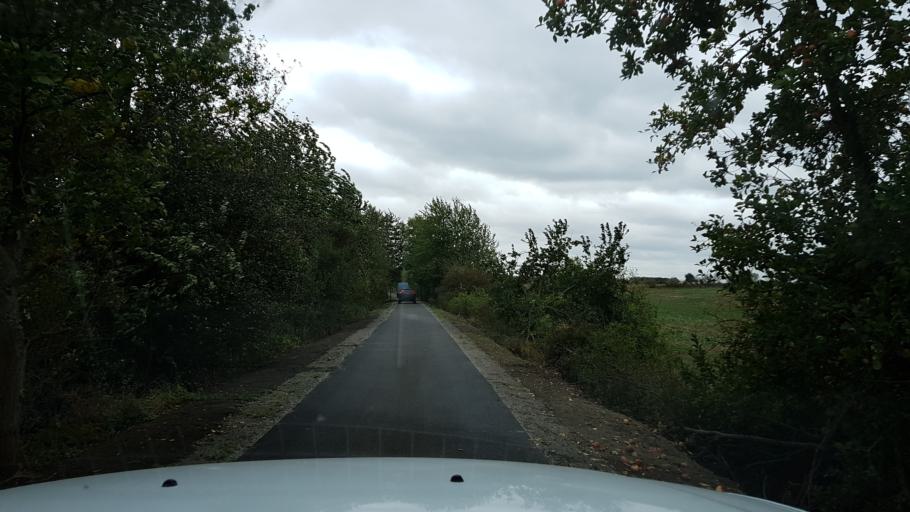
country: PL
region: West Pomeranian Voivodeship
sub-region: Powiat gryfinski
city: Cedynia
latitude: 52.8544
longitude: 14.2826
